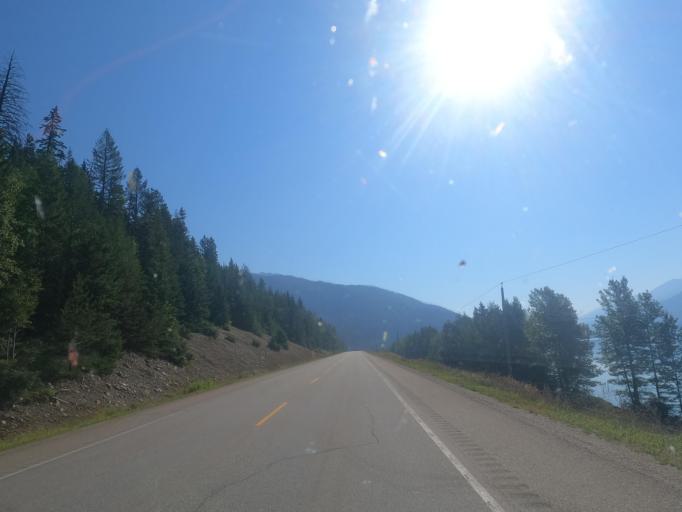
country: CA
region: Alberta
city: Jasper Park Lodge
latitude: 52.9548
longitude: -118.8860
